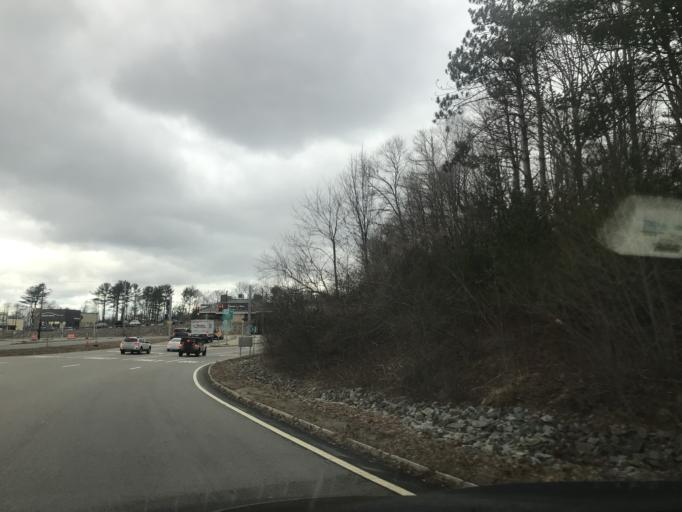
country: US
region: Massachusetts
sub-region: Plymouth County
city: North Pembroke
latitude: 42.1070
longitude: -70.7681
